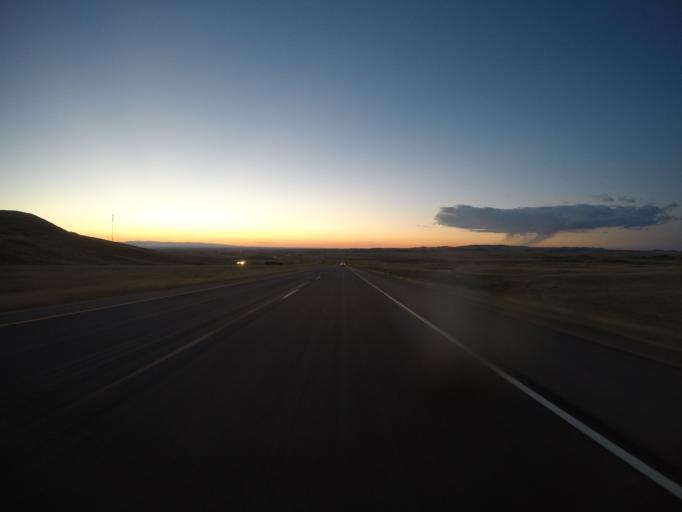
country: US
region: Wyoming
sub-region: Albany County
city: Laramie
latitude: 41.0581
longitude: -105.4726
